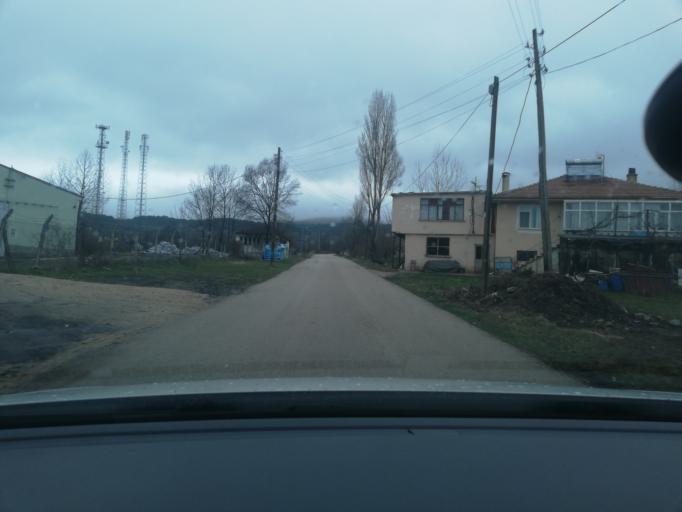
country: TR
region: Bolu
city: Bolu
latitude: 40.7306
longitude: 31.5455
